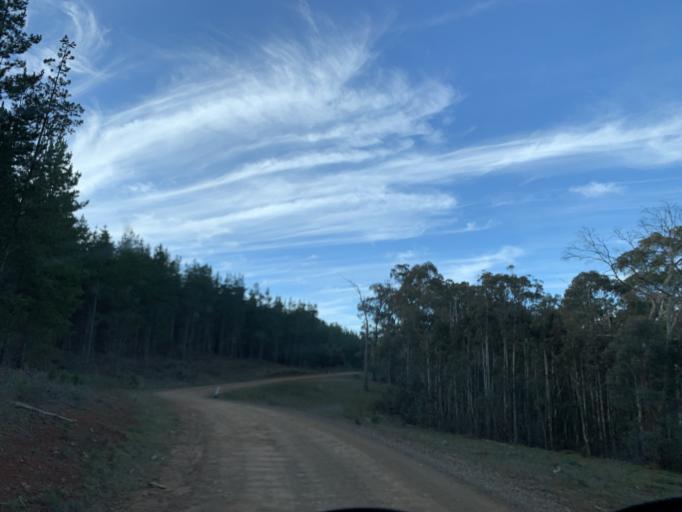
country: AU
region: Victoria
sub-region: Mansfield
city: Mansfield
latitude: -36.9189
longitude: 146.1049
